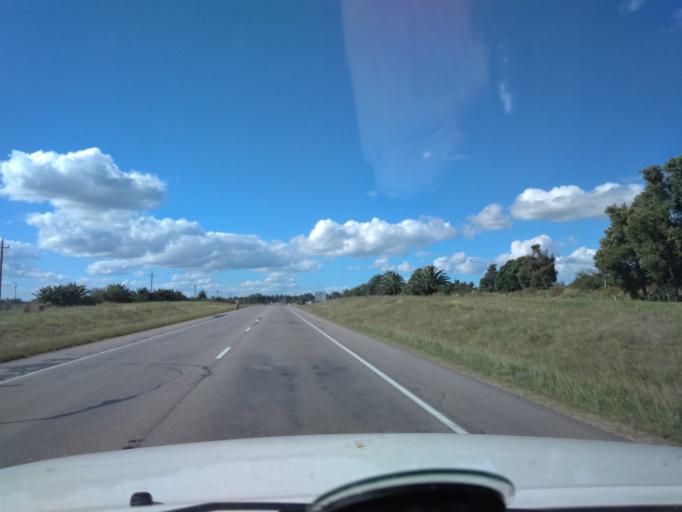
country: UY
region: Florida
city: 25 de Mayo
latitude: -34.2892
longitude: -56.2205
